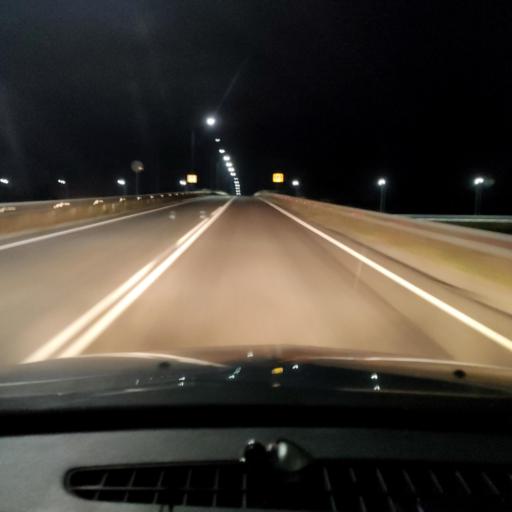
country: RU
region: Voronezj
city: Novaya Usman'
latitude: 51.6011
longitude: 39.3384
